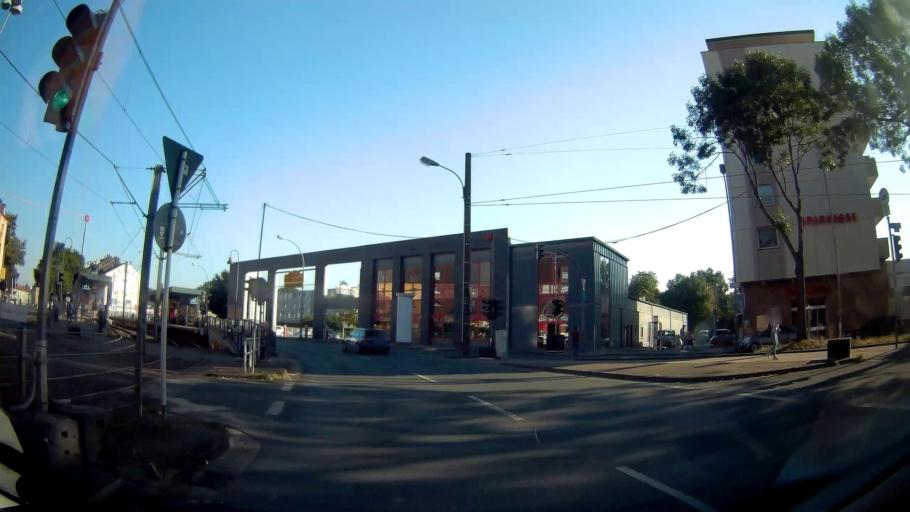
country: DE
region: North Rhine-Westphalia
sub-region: Regierungsbezirk Arnsberg
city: Dortmund
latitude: 51.5283
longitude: 7.4614
